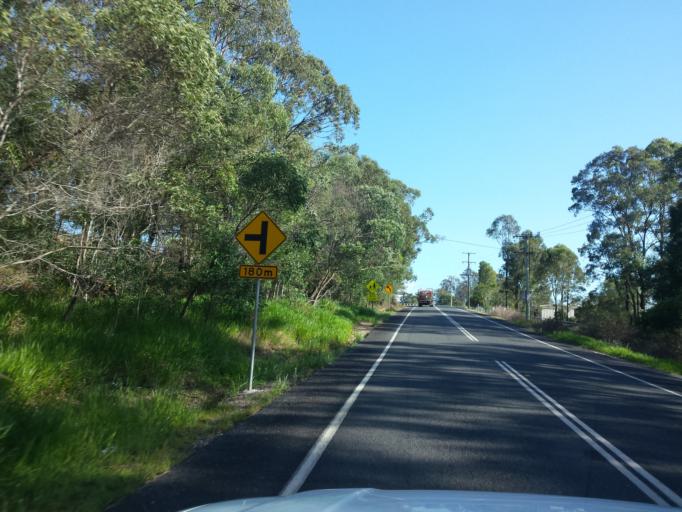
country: AU
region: Queensland
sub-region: Logan
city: Windaroo
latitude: -27.7696
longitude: 153.1910
